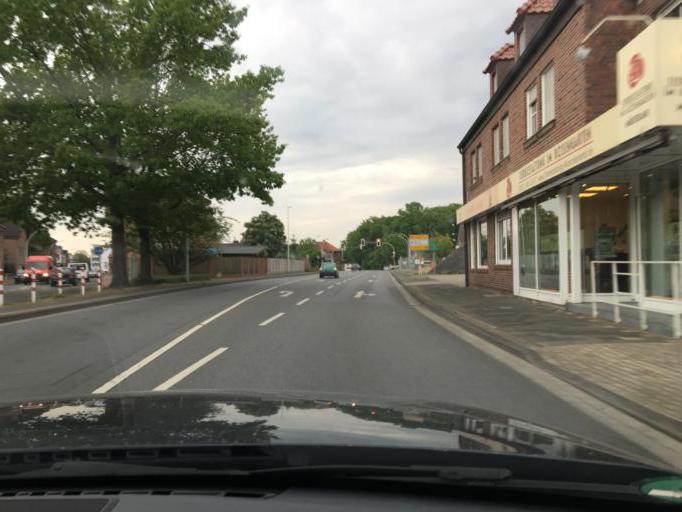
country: DE
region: North Rhine-Westphalia
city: Emsdetten
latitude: 52.1719
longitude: 7.5383
